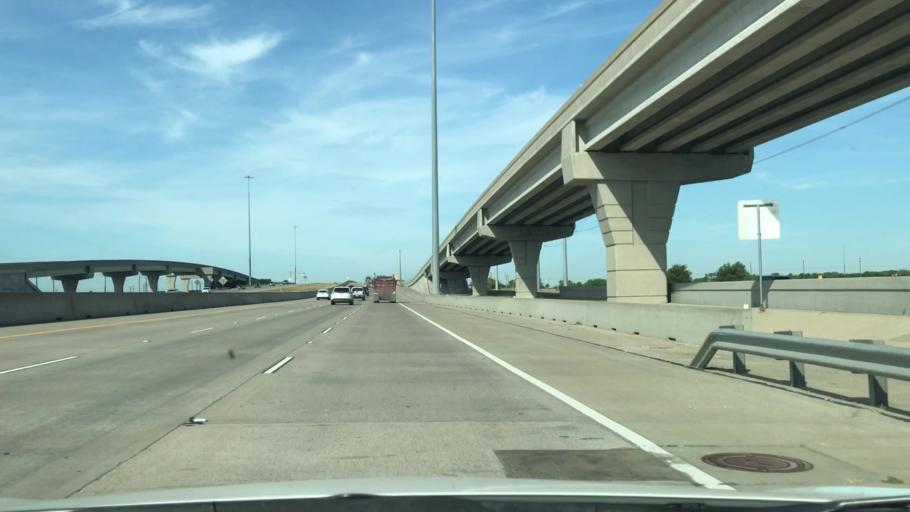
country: US
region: Texas
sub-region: Collin County
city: Fairview
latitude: 33.1532
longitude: -96.6576
